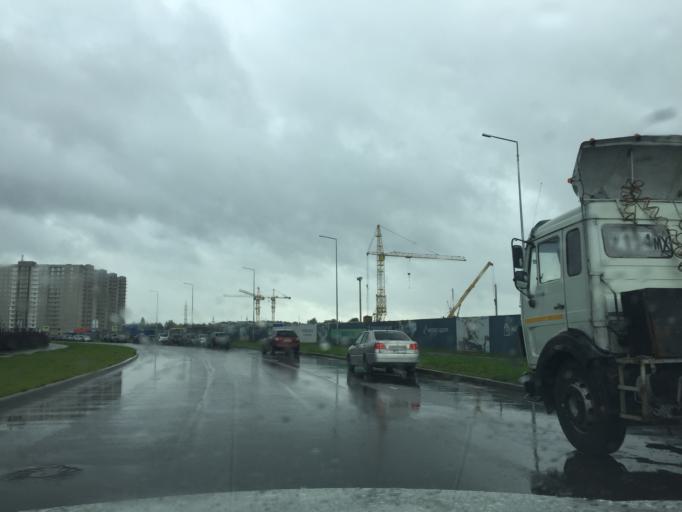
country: RU
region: St.-Petersburg
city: Gorelovo
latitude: 59.7913
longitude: 30.1629
